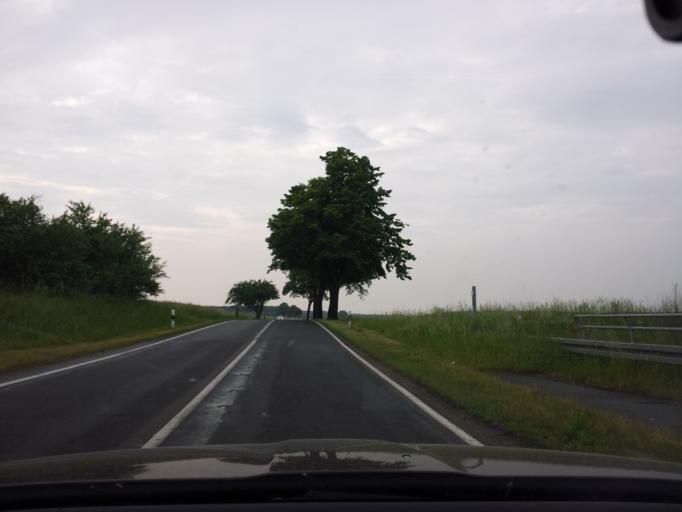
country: DE
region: Brandenburg
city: Treuenbrietzen
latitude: 52.1018
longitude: 12.8418
